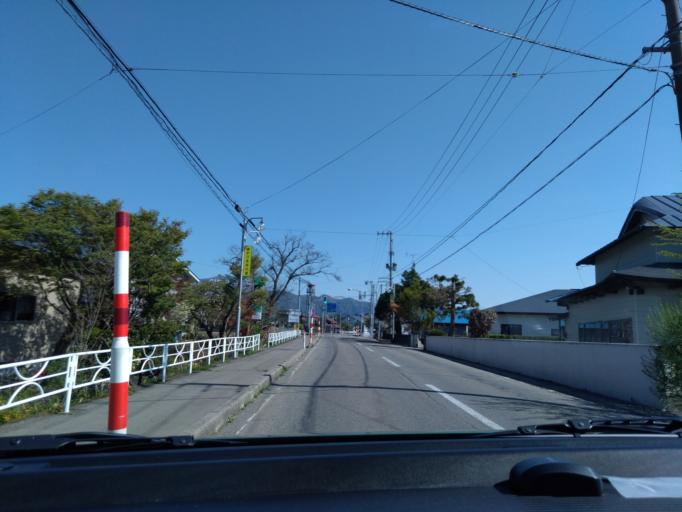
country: JP
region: Akita
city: Kakunodatemachi
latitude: 39.5091
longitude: 140.5947
